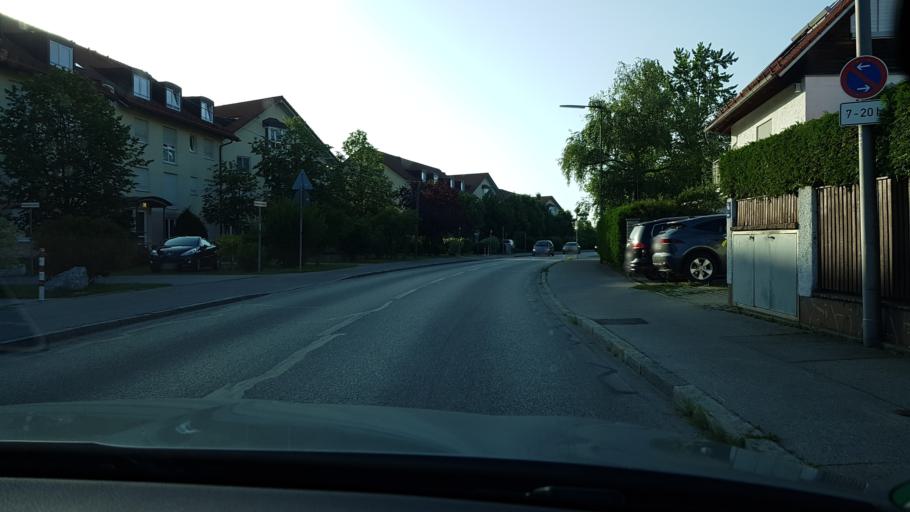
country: DE
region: Bavaria
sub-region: Upper Bavaria
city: Bogenhausen
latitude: 48.1455
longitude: 11.6595
